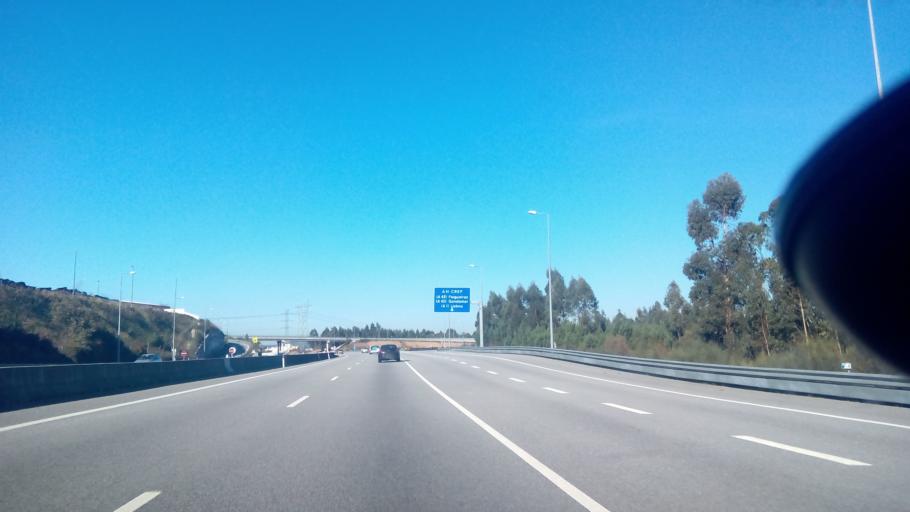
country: PT
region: Porto
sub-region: Valongo
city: Campo
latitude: 41.1772
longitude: -8.4417
